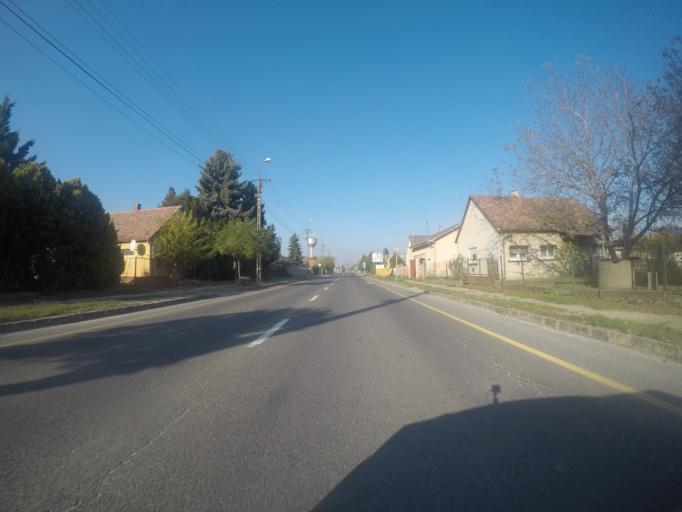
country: HU
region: Fejer
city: Ercsi
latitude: 47.2474
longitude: 18.8904
